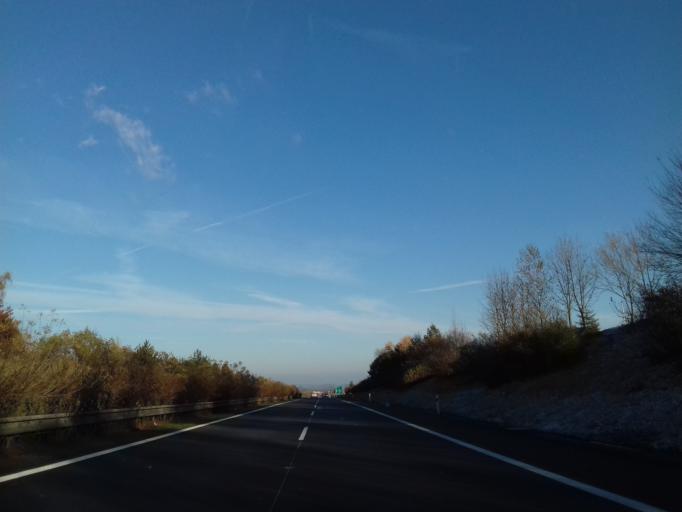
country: CZ
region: Plzensky
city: Zbiroh
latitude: 49.8380
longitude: 13.7995
